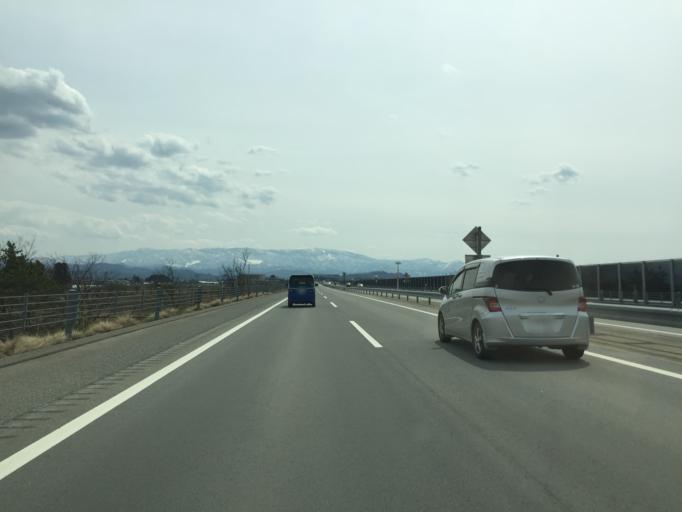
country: JP
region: Yamagata
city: Takahata
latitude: 38.0041
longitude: 140.1566
